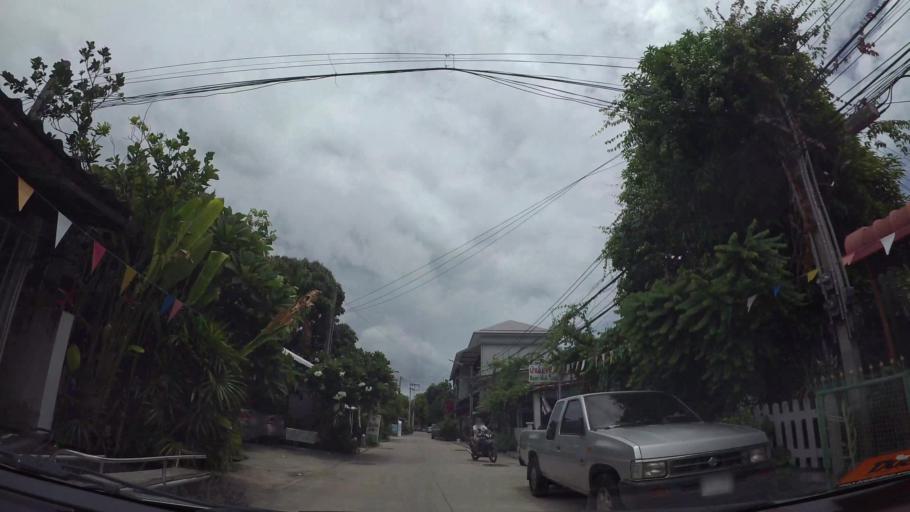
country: TH
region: Chon Buri
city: Sattahip
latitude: 12.7618
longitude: 100.8862
